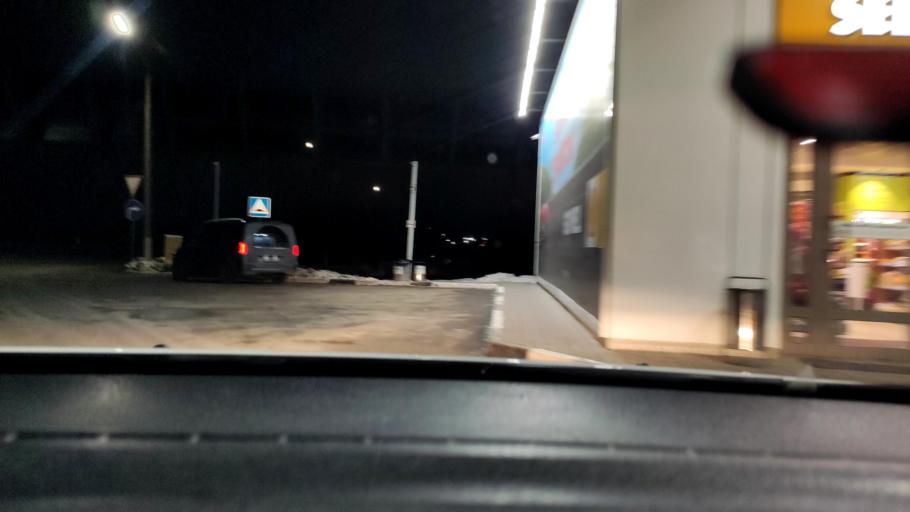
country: RU
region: Voronezj
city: Ramon'
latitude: 51.9228
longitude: 39.2197
